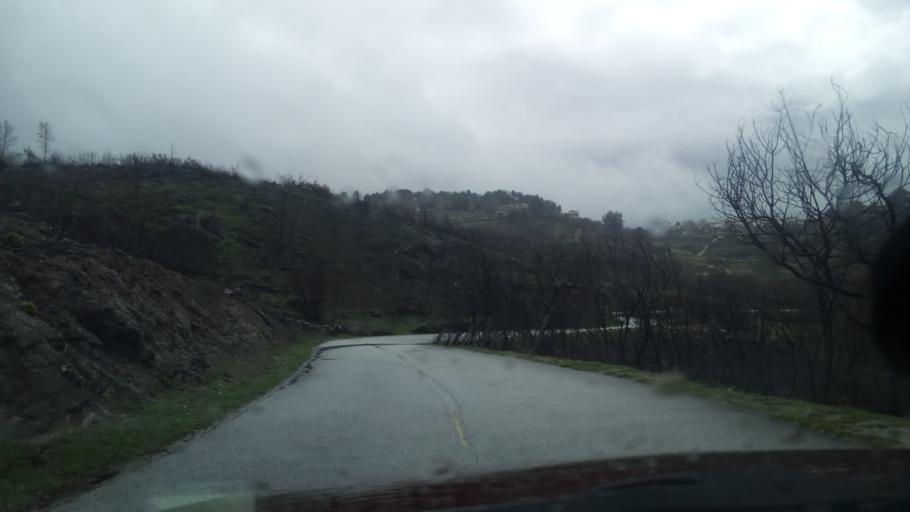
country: PT
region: Guarda
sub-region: Fornos de Algodres
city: Fornos de Algodres
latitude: 40.5494
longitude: -7.4777
